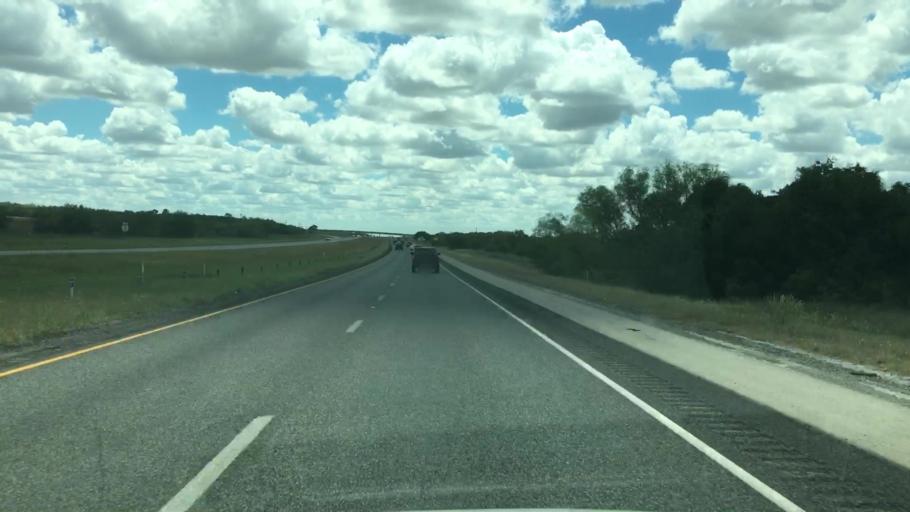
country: US
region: Texas
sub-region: Atascosa County
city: Poteet
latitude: 29.1158
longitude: -98.4321
